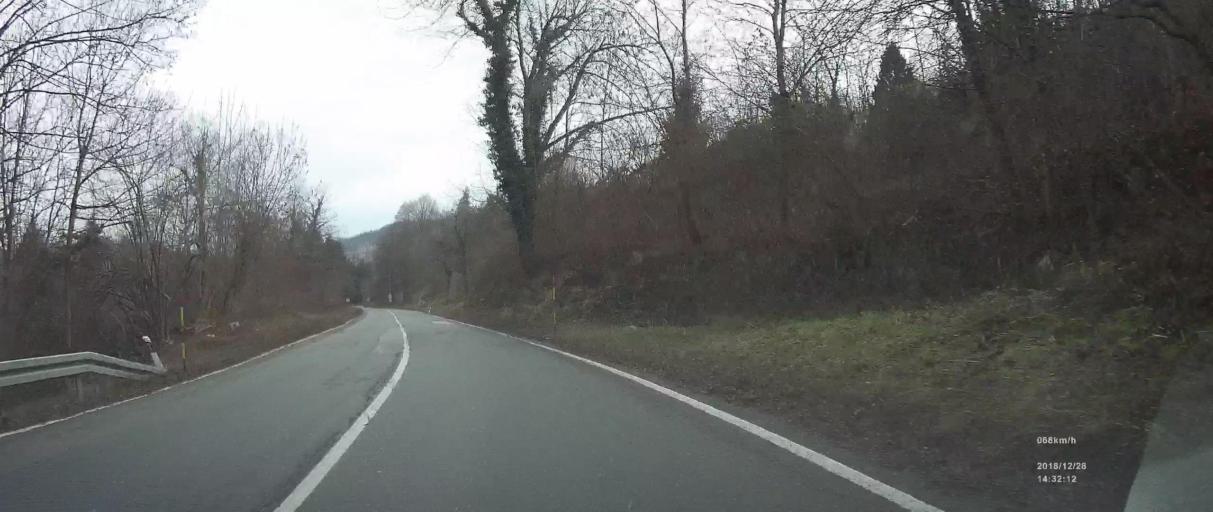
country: HR
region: Primorsko-Goranska
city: Vrbovsko
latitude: 45.4134
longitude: 15.1526
